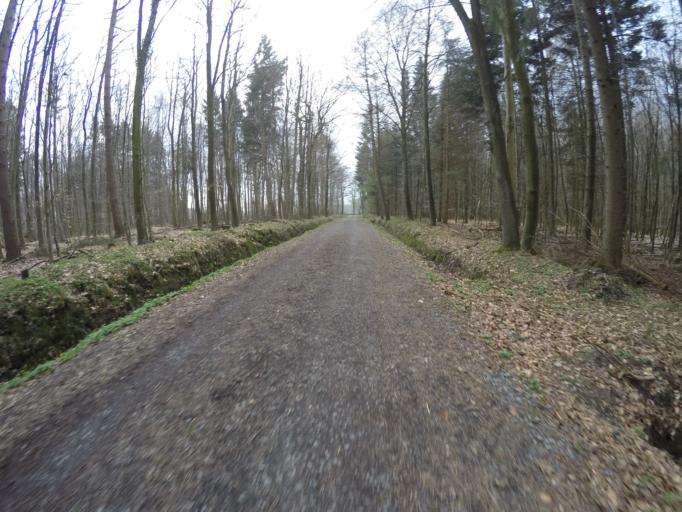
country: DE
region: Schleswig-Holstein
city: Borstel-Hohenraden
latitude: 53.7205
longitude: 9.8092
